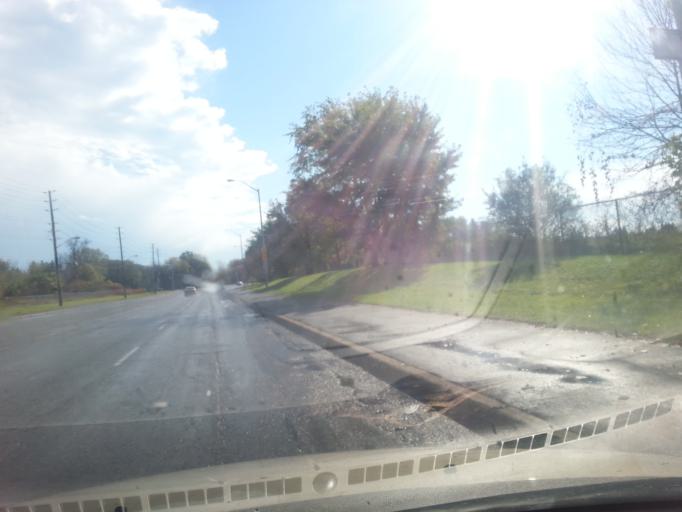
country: CA
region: Ontario
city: Bells Corners
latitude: 45.3435
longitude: -75.8110
